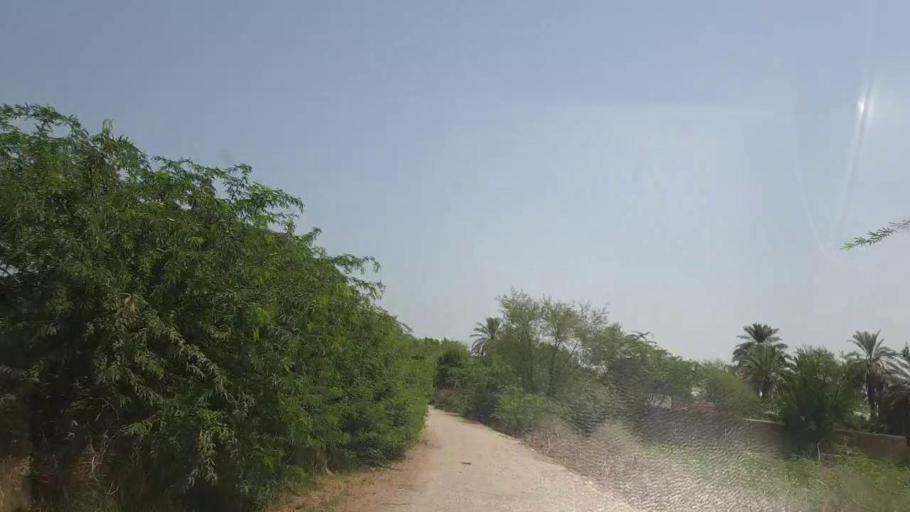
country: PK
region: Sindh
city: Kot Diji
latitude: 27.2843
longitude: 68.6405
